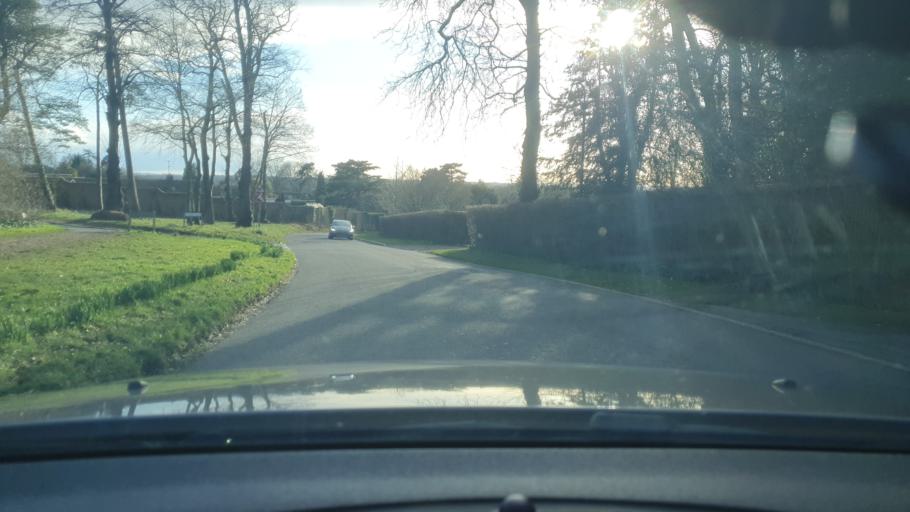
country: GB
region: England
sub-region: Wokingham
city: Wargrave
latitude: 51.5042
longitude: -0.8651
